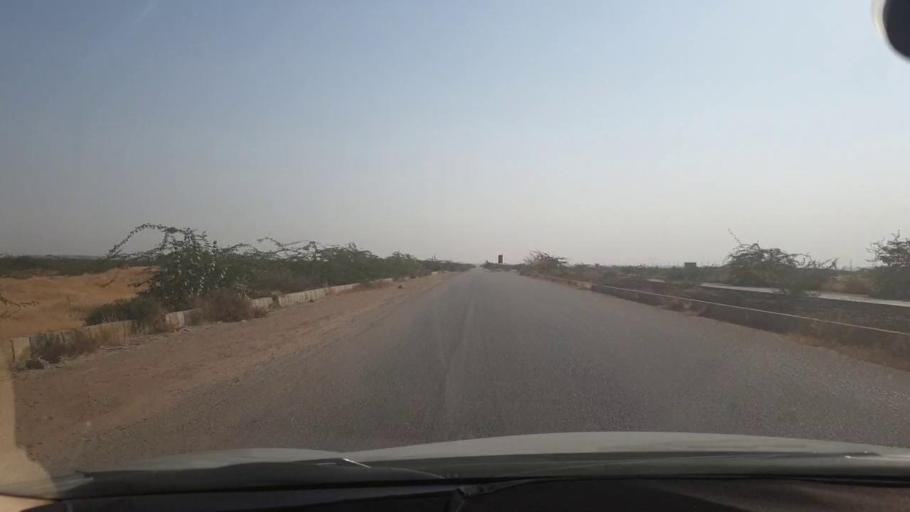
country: PK
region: Sindh
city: Malir Cantonment
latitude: 25.0736
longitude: 67.1385
